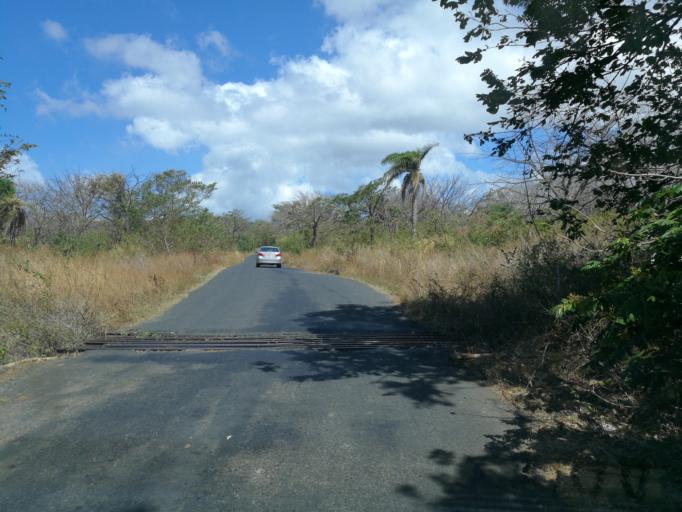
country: CR
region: Guanacaste
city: Liberia
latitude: 10.7518
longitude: -85.3718
